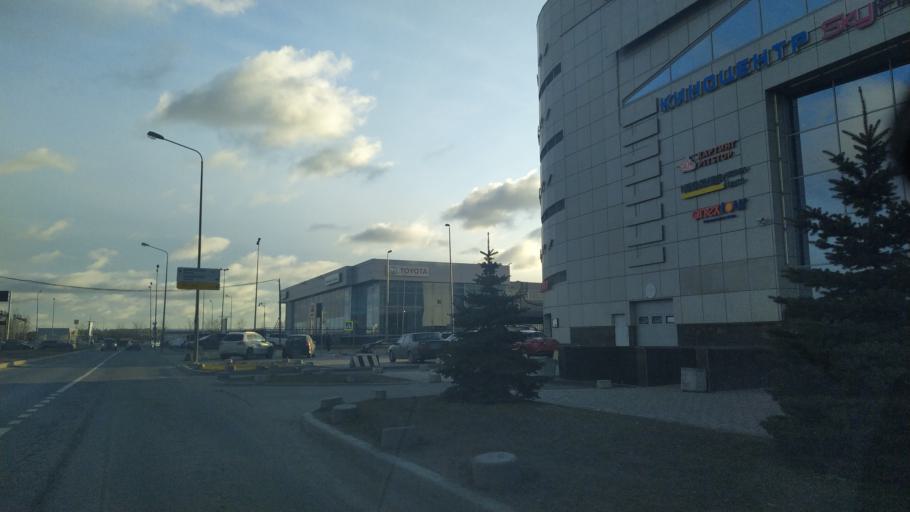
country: RU
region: St.-Petersburg
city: Kupchino
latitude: 59.8059
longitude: 30.3219
